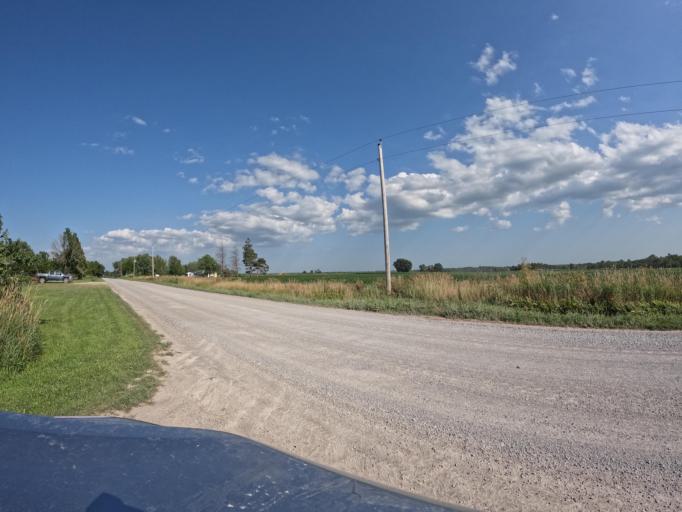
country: US
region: Iowa
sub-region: Appanoose County
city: Centerville
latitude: 40.7175
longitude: -93.0333
